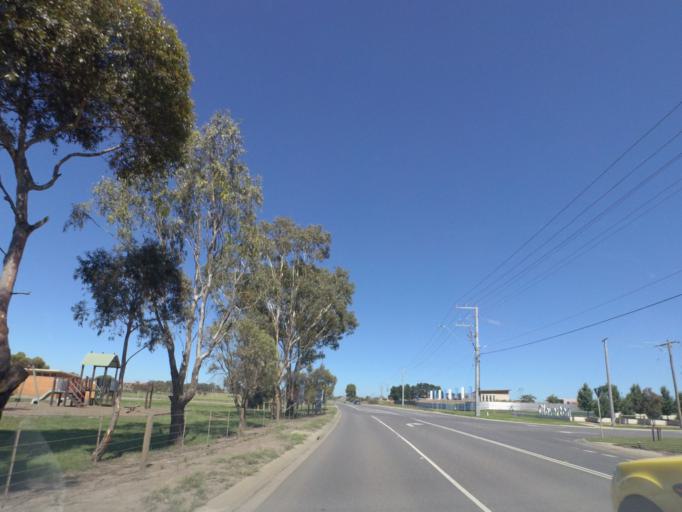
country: AU
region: Victoria
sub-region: Hume
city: Craigieburn
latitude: -37.5412
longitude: 144.9548
